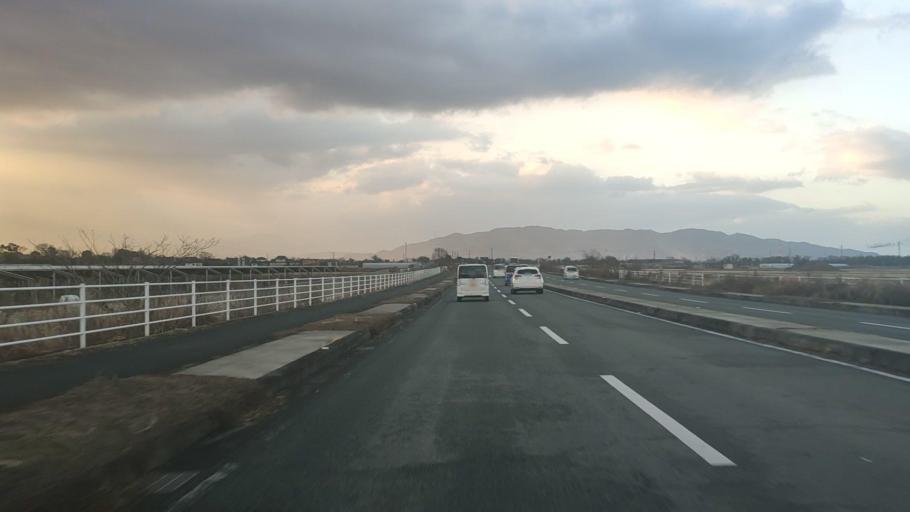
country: JP
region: Kumamoto
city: Kumamoto
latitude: 32.7520
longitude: 130.7067
